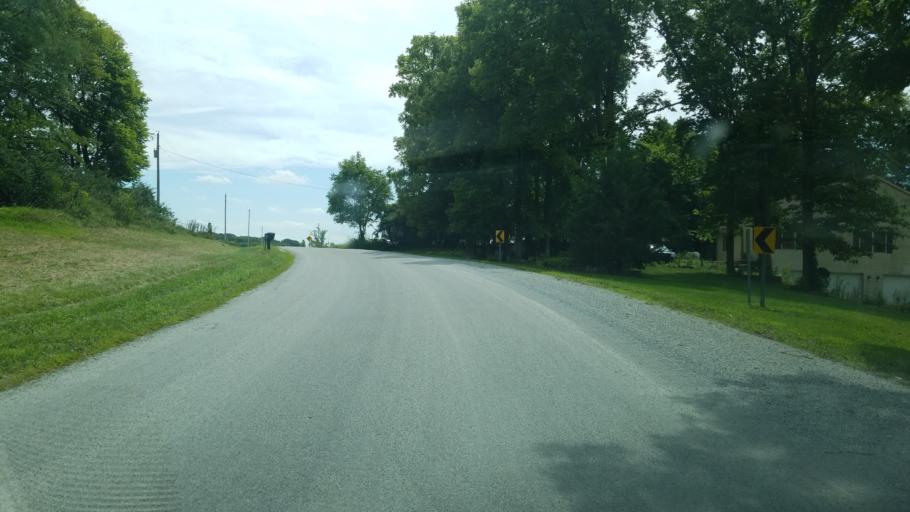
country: US
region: Ohio
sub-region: Hardin County
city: Kenton
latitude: 40.5810
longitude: -83.5056
